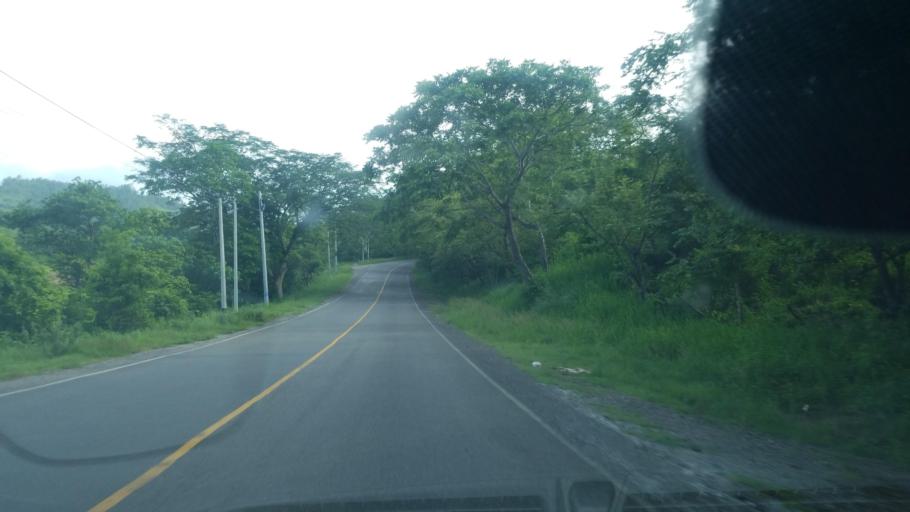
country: HN
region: Santa Barbara
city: Ilama
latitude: 15.1021
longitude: -88.2000
